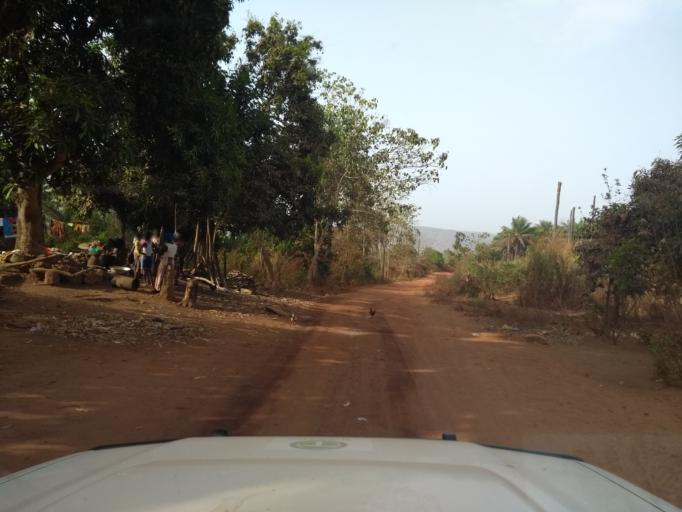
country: GN
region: Kindia
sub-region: Prefecture de Dubreka
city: Dubreka
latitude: 9.8777
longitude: -13.5411
